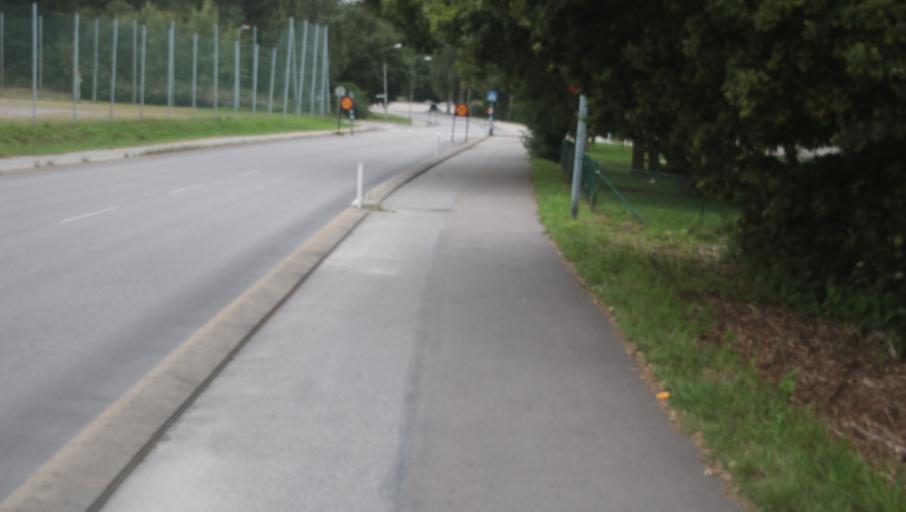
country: SE
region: Blekinge
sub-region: Karlshamns Kommun
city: Karlshamn
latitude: 56.1649
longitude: 14.8833
